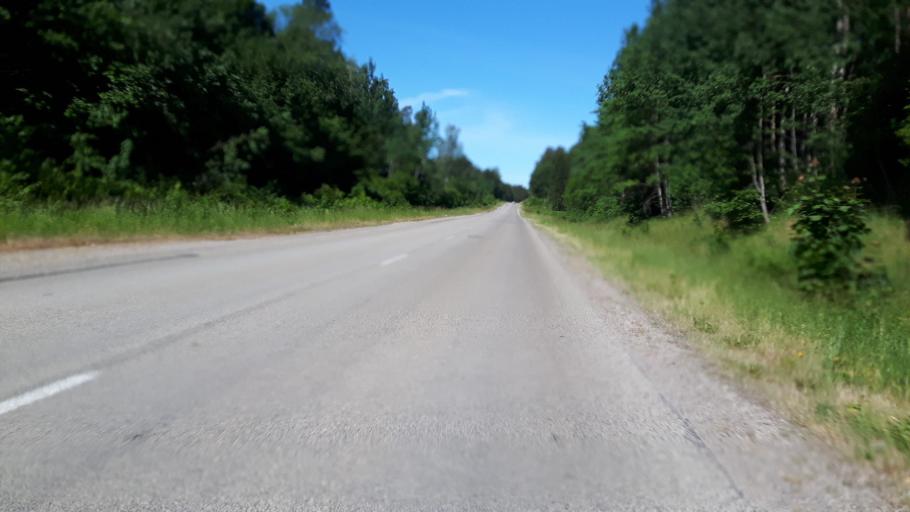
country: LV
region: Tukuma Rajons
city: Tukums
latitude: 57.0041
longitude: 23.0758
